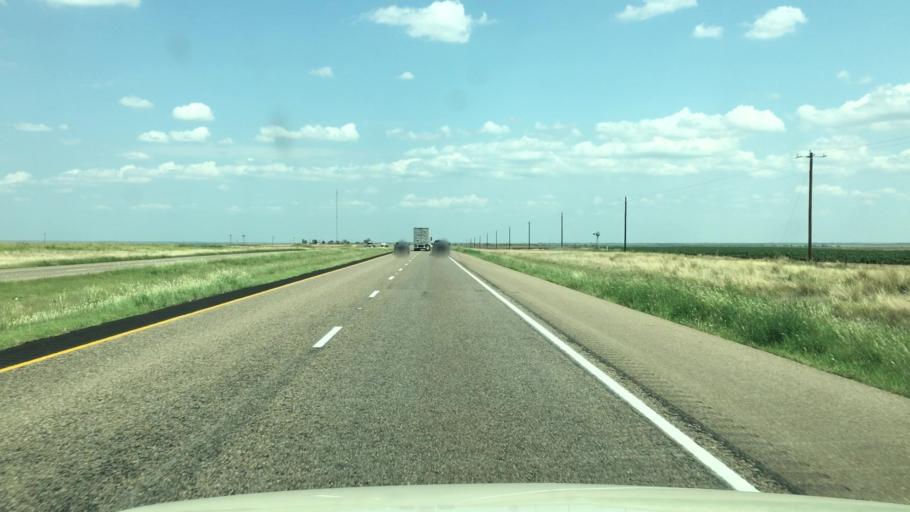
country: US
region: Texas
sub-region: Armstrong County
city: Claude
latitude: 35.0333
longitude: -101.1659
